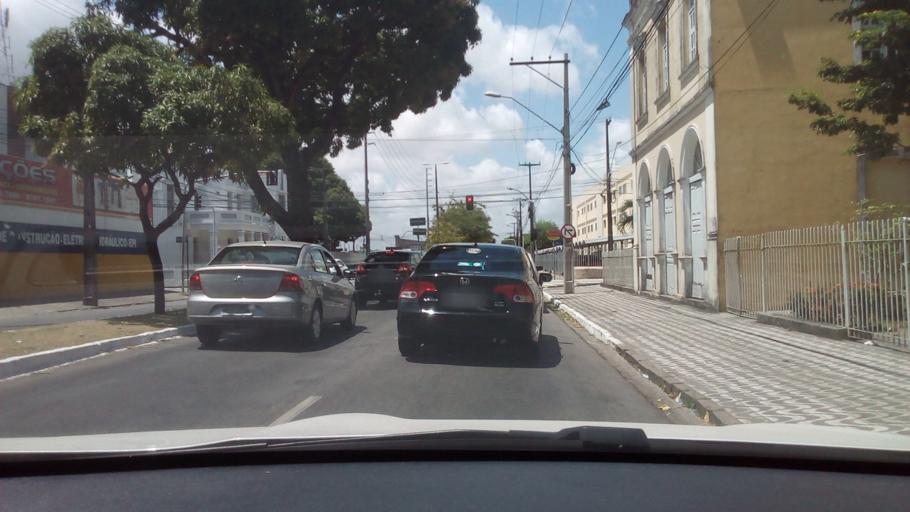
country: BR
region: Paraiba
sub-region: Joao Pessoa
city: Joao Pessoa
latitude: -7.1258
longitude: -34.8842
